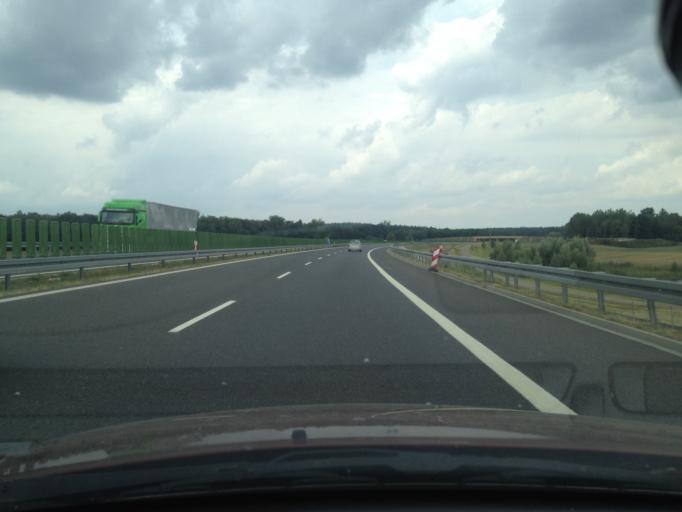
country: PL
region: West Pomeranian Voivodeship
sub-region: Powiat mysliborski
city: Mysliborz
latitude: 52.9885
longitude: 14.8696
